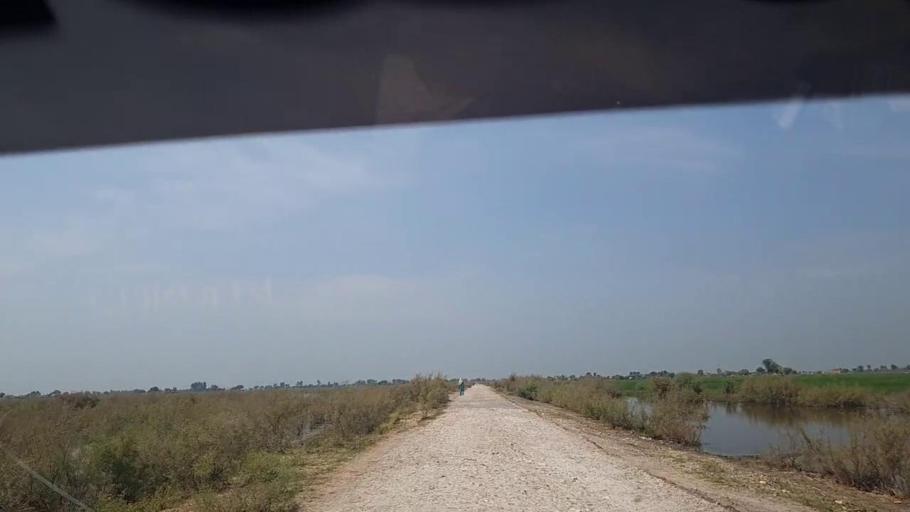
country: PK
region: Sindh
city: Thul
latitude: 28.1682
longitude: 68.7625
